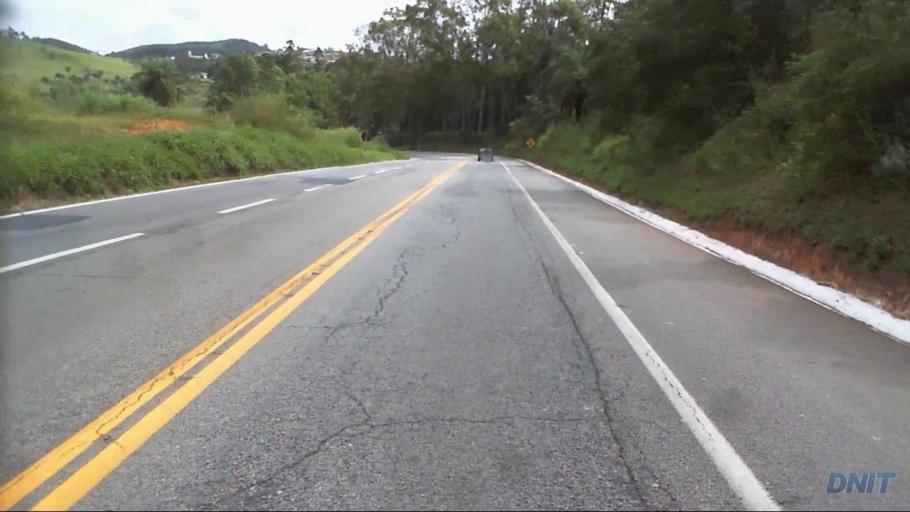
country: BR
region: Minas Gerais
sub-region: Caete
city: Caete
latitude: -19.7245
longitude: -43.5708
